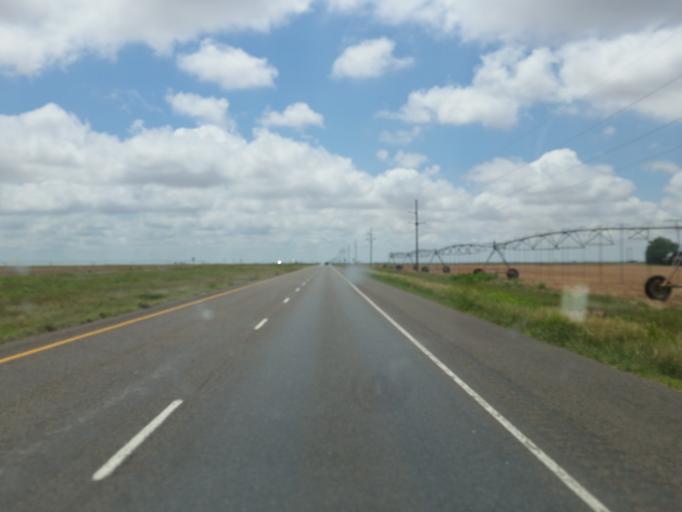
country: US
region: Texas
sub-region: Lubbock County
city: Slaton
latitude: 33.3938
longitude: -101.6040
